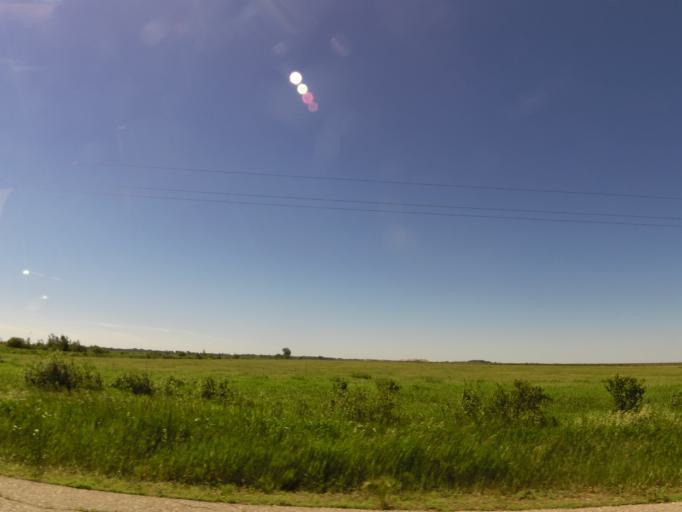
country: US
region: Minnesota
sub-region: Red Lake County
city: Red Lake Falls
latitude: 47.7600
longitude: -96.2897
